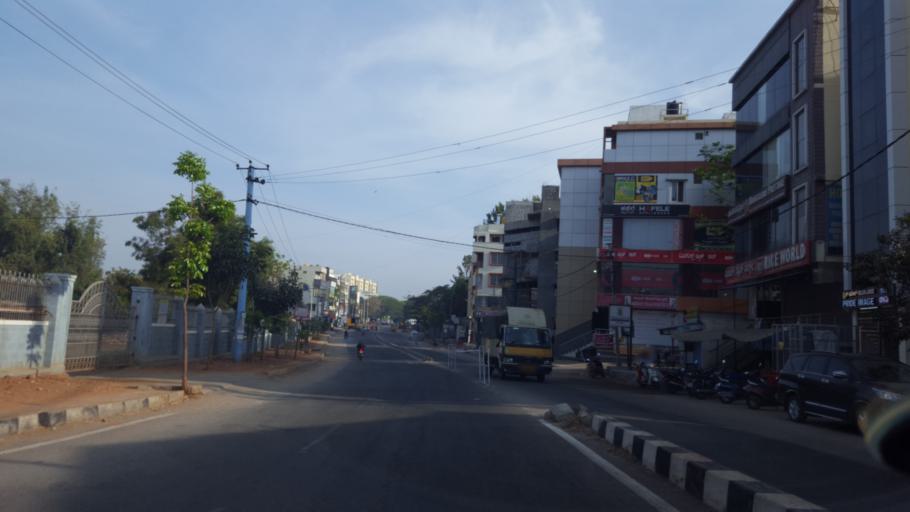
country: IN
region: Karnataka
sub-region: Bangalore Urban
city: Bangalore
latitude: 12.9130
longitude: 77.5137
